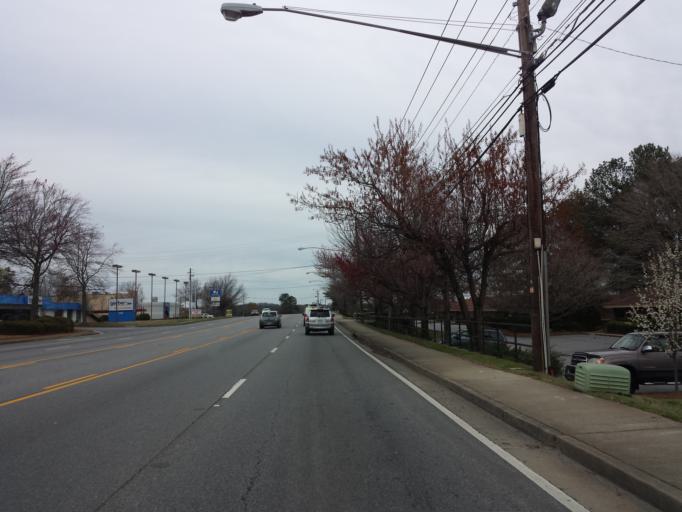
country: US
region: Georgia
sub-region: Fulton County
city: Roswell
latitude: 34.0522
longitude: -84.3336
